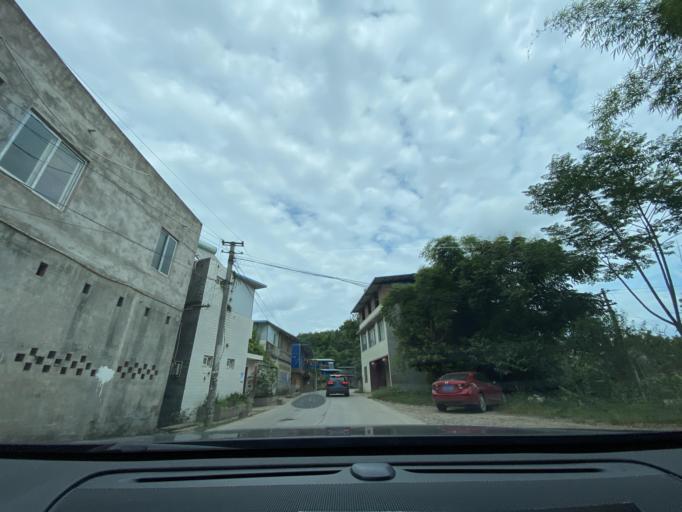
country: CN
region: Sichuan
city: Jiancheng
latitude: 30.4415
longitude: 104.5425
